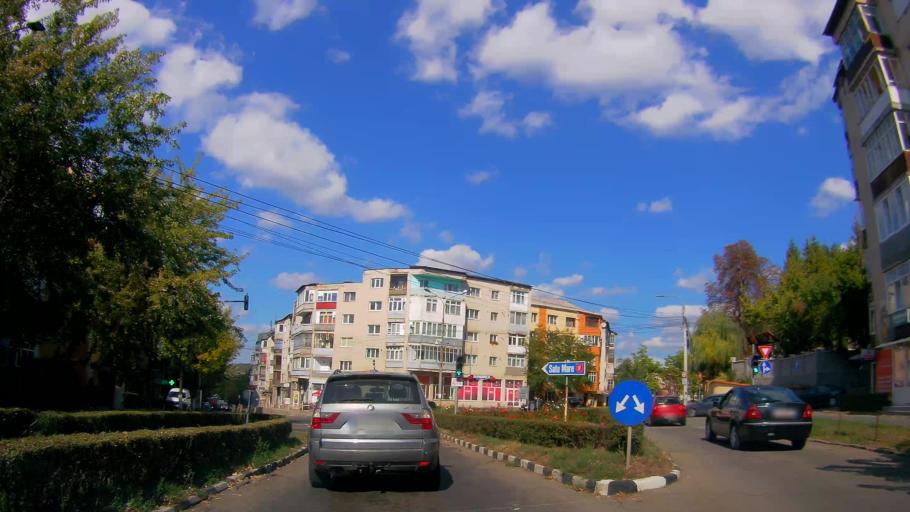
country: RO
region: Salaj
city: Zalau
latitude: 47.1886
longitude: 23.0618
